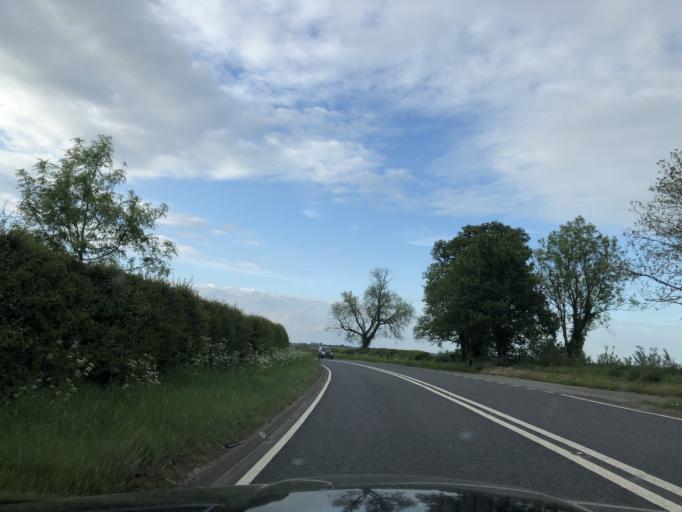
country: GB
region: England
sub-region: Gloucestershire
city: Moreton in Marsh
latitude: 52.0122
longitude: -1.6905
